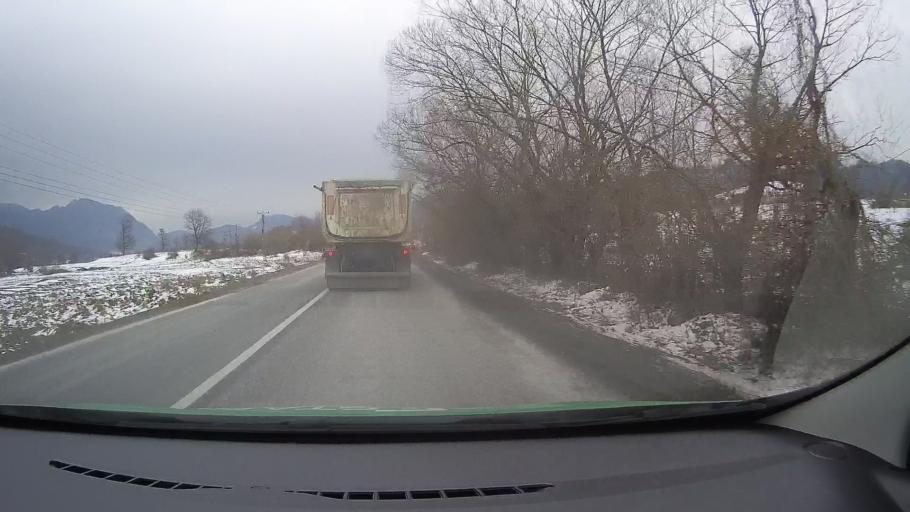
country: RO
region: Brasov
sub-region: Oras Rasnov
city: Rasnov
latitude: 45.5616
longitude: 25.4634
